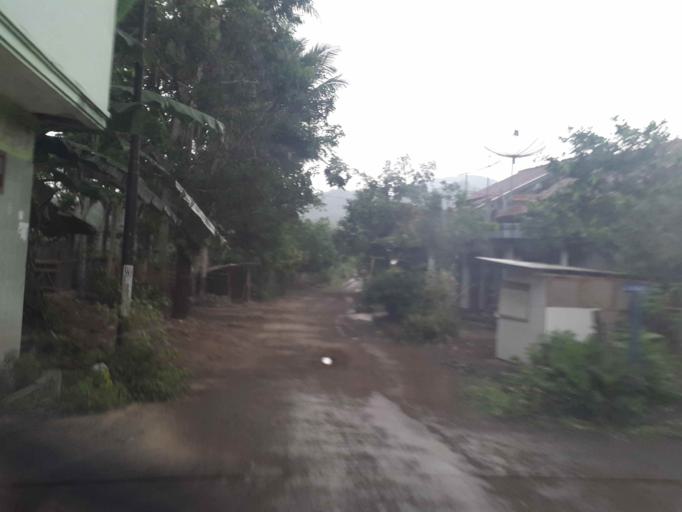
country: ID
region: Central Java
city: Genteng Wetan
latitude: -7.3616
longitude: 108.8645
